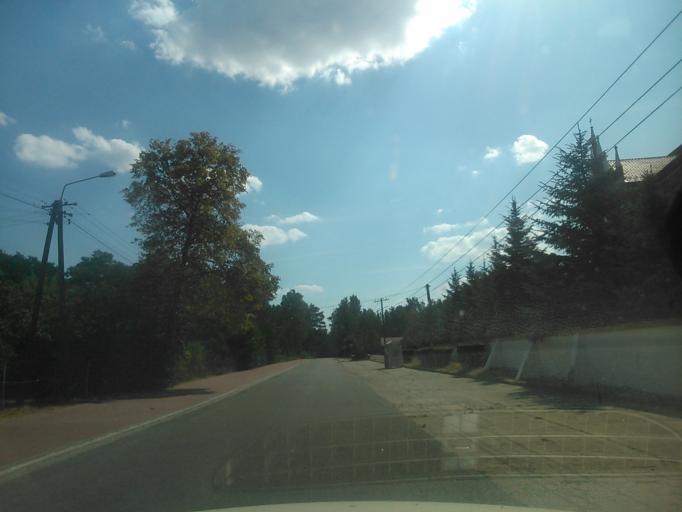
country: PL
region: Masovian Voivodeship
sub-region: Powiat ostrolecki
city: Czarnia
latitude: 53.3543
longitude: 21.2052
